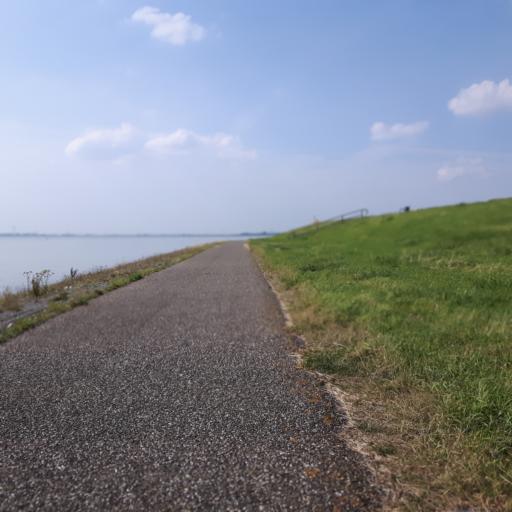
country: NL
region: Zeeland
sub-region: Gemeente Reimerswaal
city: Yerseke
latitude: 51.4466
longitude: 4.0002
